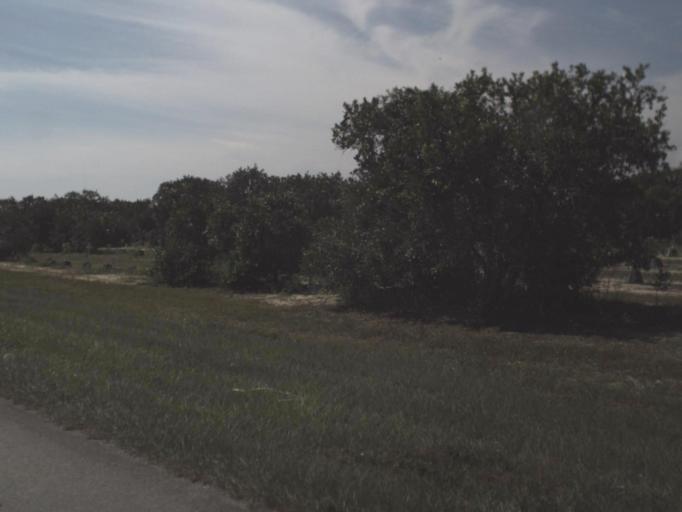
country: US
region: Florida
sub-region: Highlands County
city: Sebring
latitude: 27.5274
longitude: -81.4535
